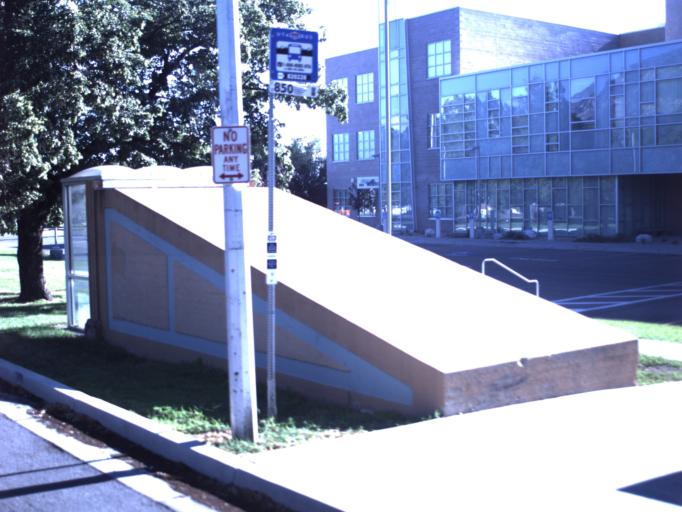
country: US
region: Utah
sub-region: Utah County
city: Provo
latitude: 40.2401
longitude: -111.6675
